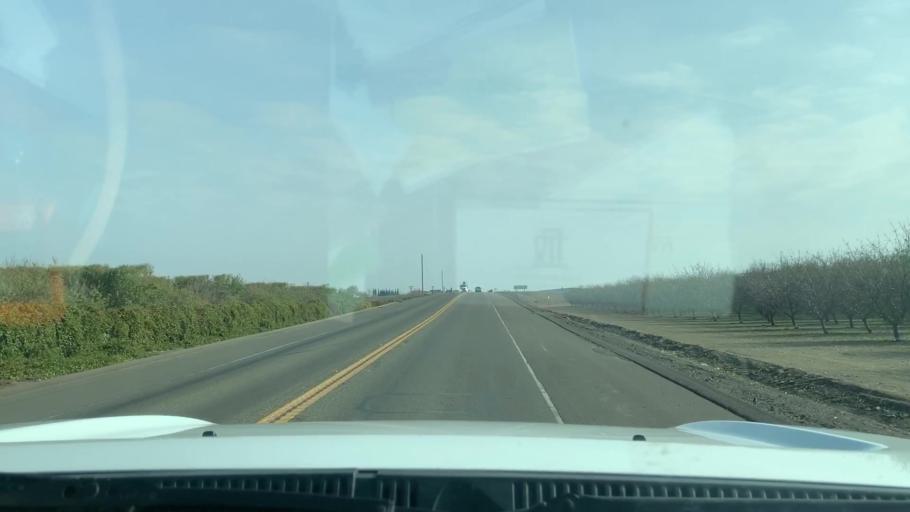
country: US
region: California
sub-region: Fresno County
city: Huron
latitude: 36.2553
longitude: -120.0933
